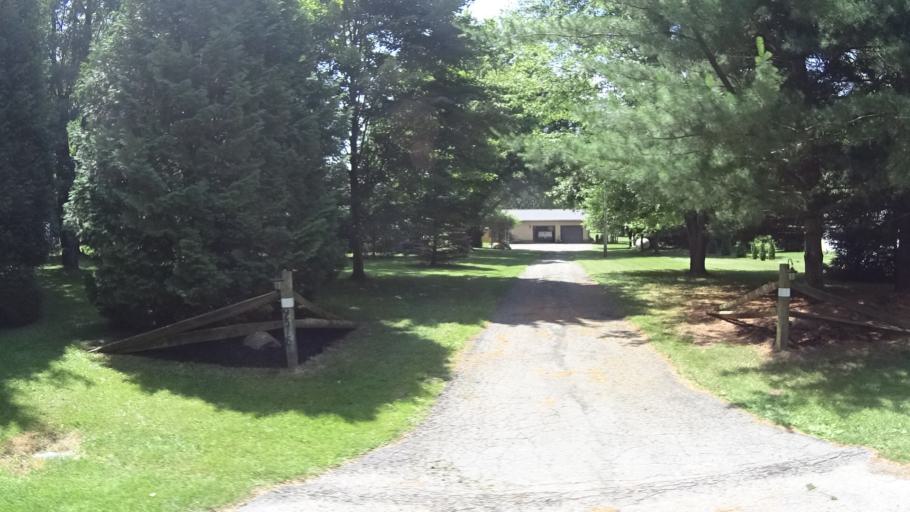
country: US
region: Ohio
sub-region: Erie County
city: Huron
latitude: 41.3533
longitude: -82.4559
